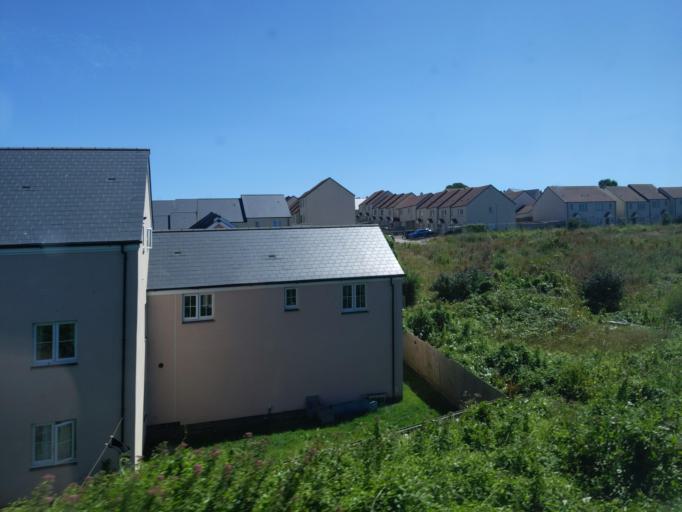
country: GB
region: England
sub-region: Cornwall
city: Hayle
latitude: 50.1891
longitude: -5.4079
